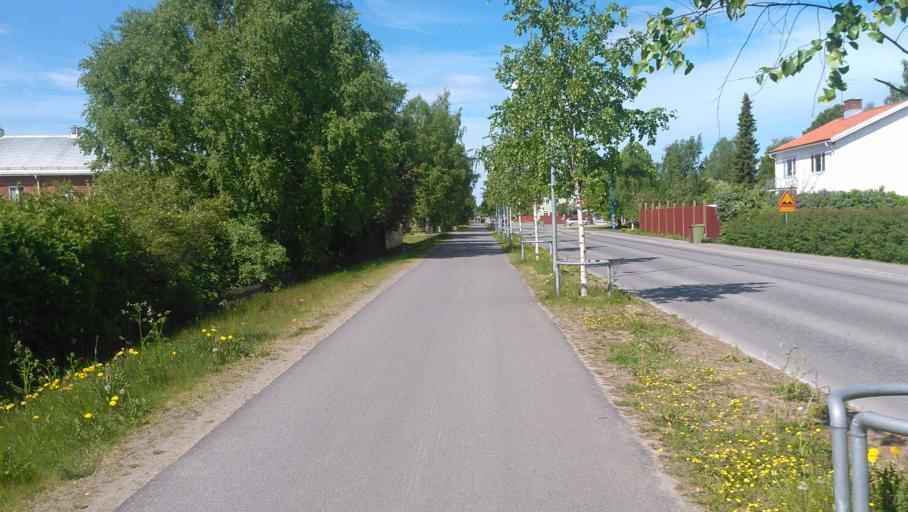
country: SE
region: Vaesterbotten
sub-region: Umea Kommun
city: Roback
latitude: 63.8334
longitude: 20.2132
